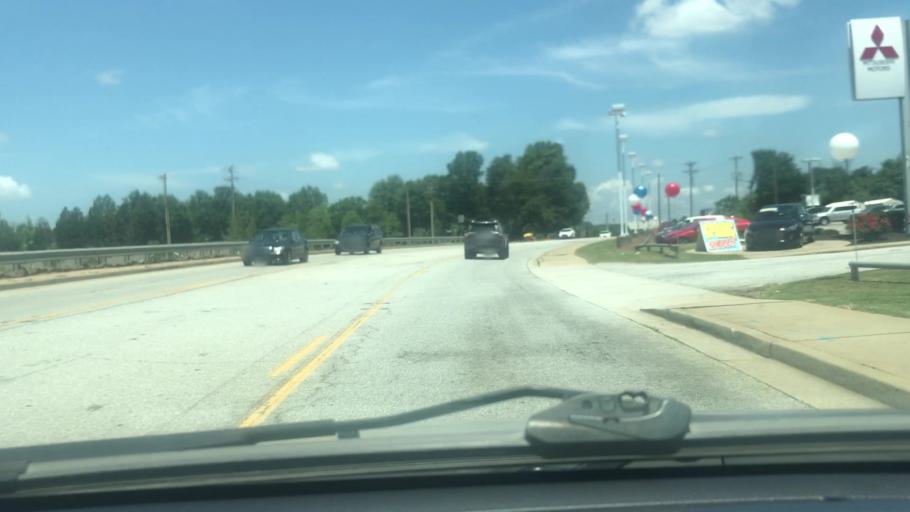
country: US
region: South Carolina
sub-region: Greenville County
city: Mauldin
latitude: 34.8406
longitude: -82.3183
